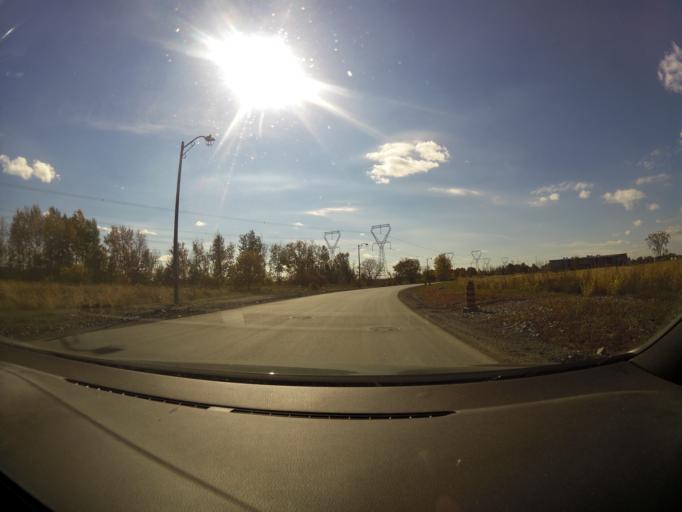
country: CA
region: Ontario
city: Bells Corners
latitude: 45.2763
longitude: -75.8936
